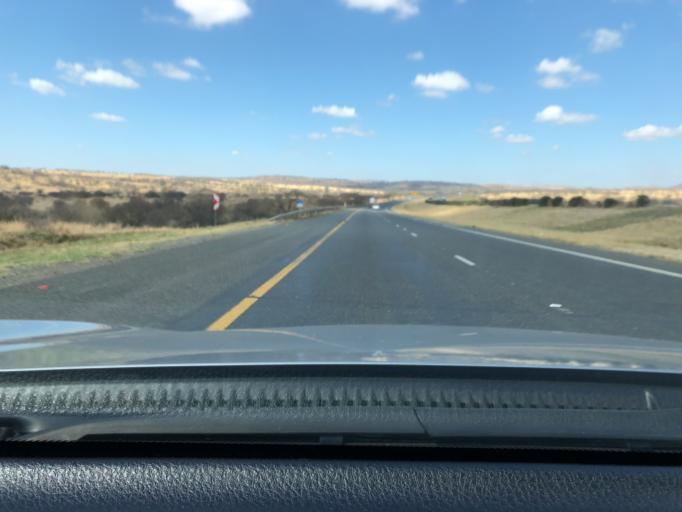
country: ZA
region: KwaZulu-Natal
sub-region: uThukela District Municipality
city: Estcourt
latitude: -28.9476
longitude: 29.7923
